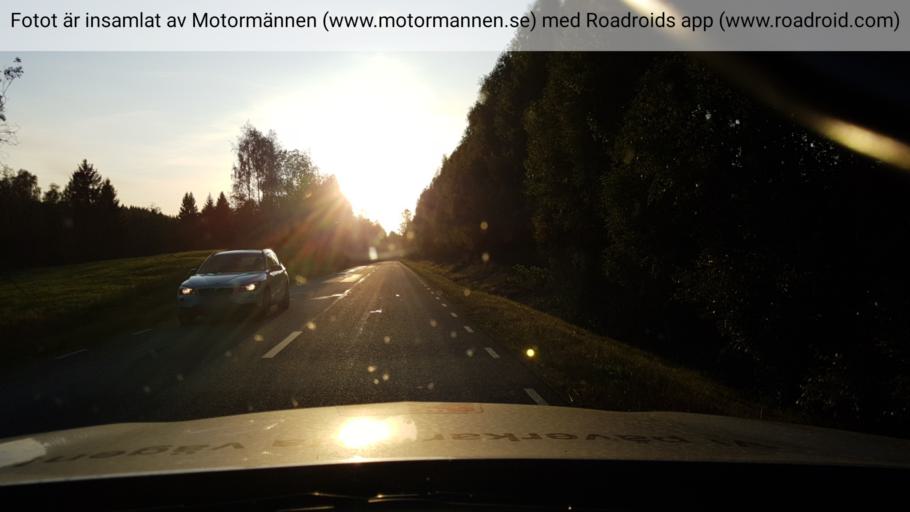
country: SE
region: Vaestmanland
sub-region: Skinnskattebergs Kommun
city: Skinnskatteberg
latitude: 59.8950
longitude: 15.5855
